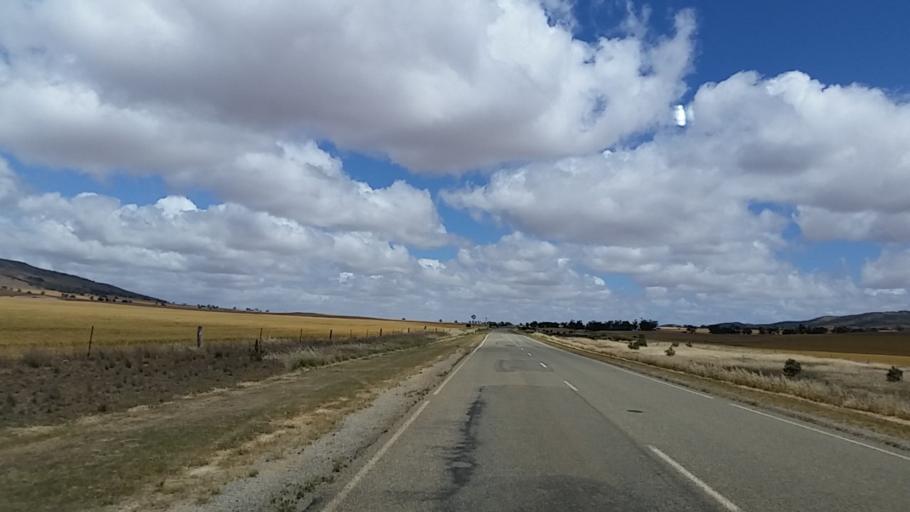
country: AU
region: South Australia
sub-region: Peterborough
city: Peterborough
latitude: -32.8511
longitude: 138.5470
